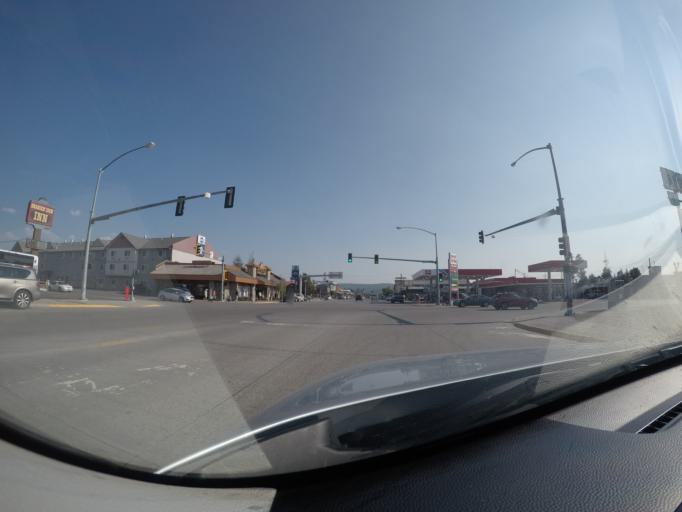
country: US
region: Montana
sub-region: Gallatin County
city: West Yellowstone
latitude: 44.6625
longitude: -111.0998
